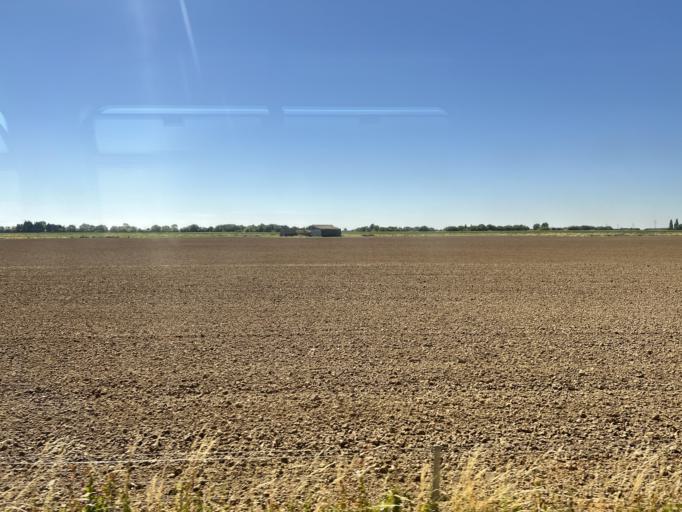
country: GB
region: England
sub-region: Lincolnshire
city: Wainfleet All Saints
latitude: 53.1173
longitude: 0.2084
